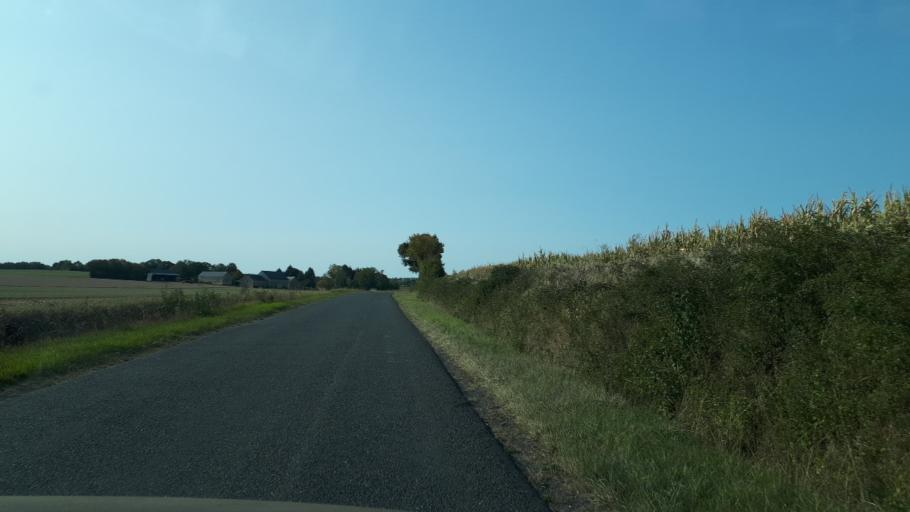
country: FR
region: Centre
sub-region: Departement du Cher
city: Rians
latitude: 47.2078
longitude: 2.5588
